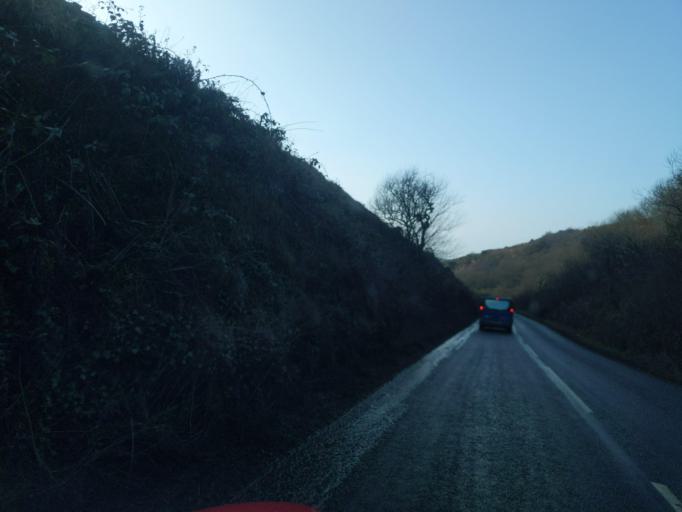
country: GB
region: England
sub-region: Cornwall
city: Tintagel
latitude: 50.6432
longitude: -4.7199
